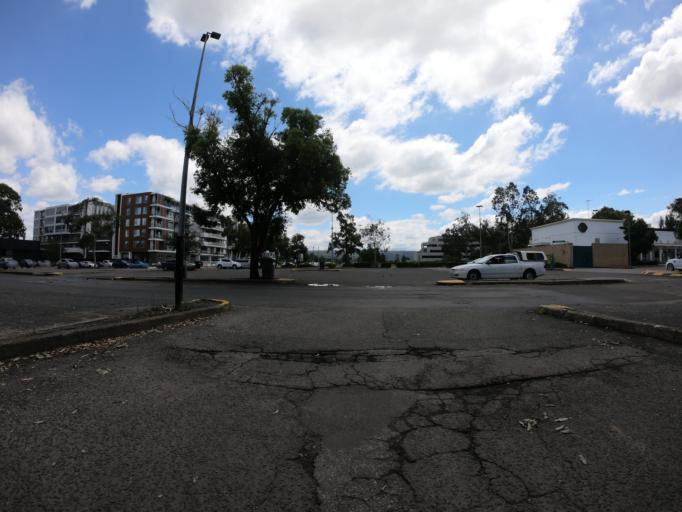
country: AU
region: New South Wales
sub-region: Penrith Municipality
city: Penrith
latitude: -33.7595
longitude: 150.6839
